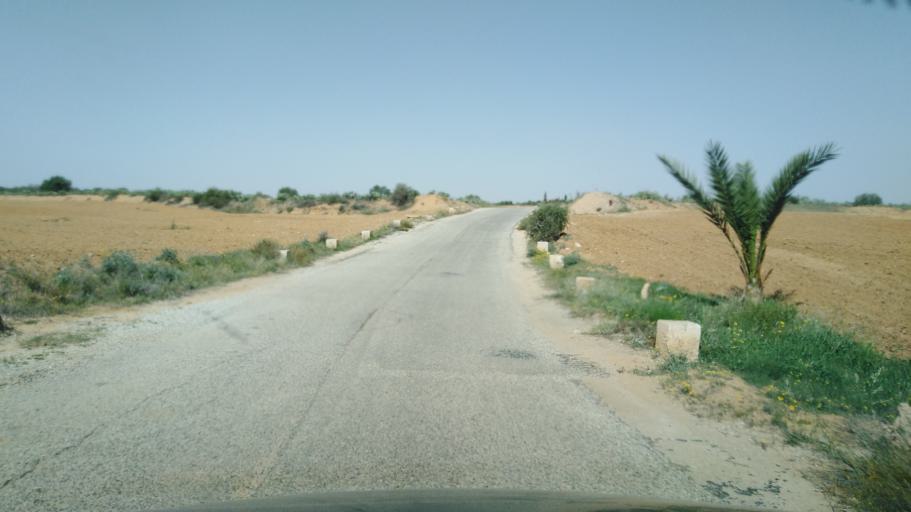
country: TN
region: Safaqis
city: Bi'r `Ali Bin Khalifah
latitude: 34.6786
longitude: 10.4133
